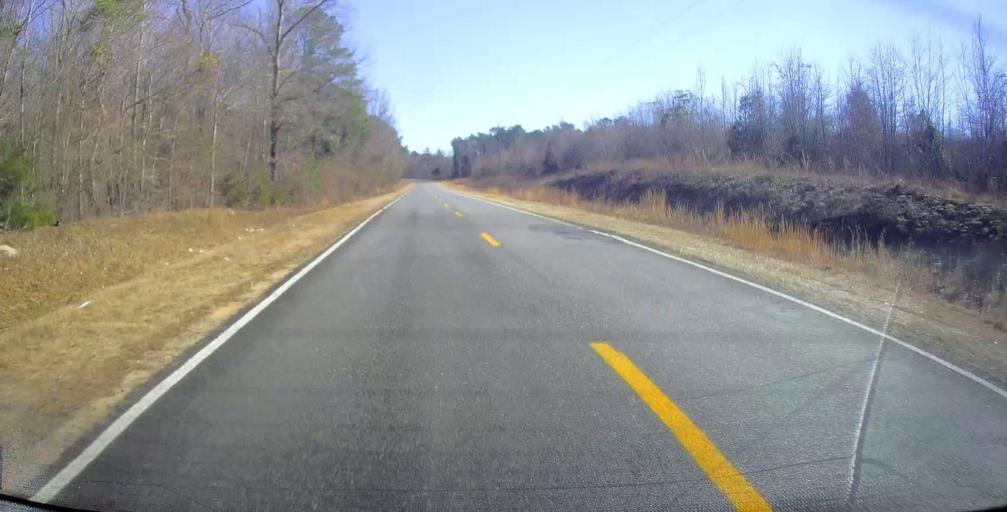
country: US
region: Georgia
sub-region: Crawford County
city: Knoxville
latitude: 32.7044
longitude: -83.9927
